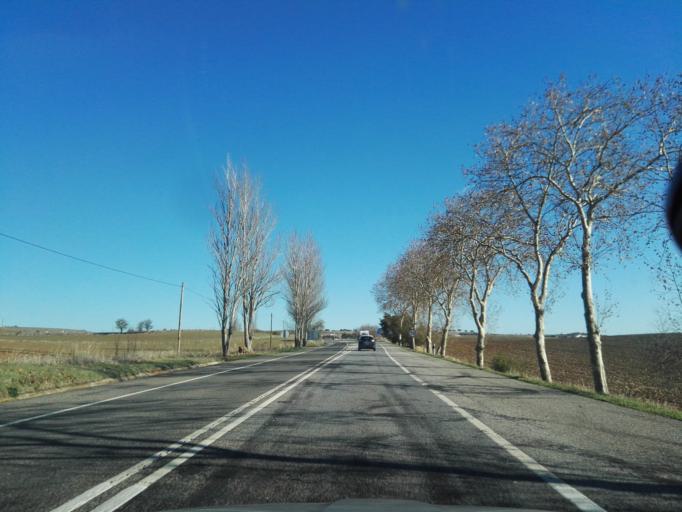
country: PT
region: Evora
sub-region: Vila Vicosa
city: Vila Vicosa
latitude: 38.8472
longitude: -7.3612
